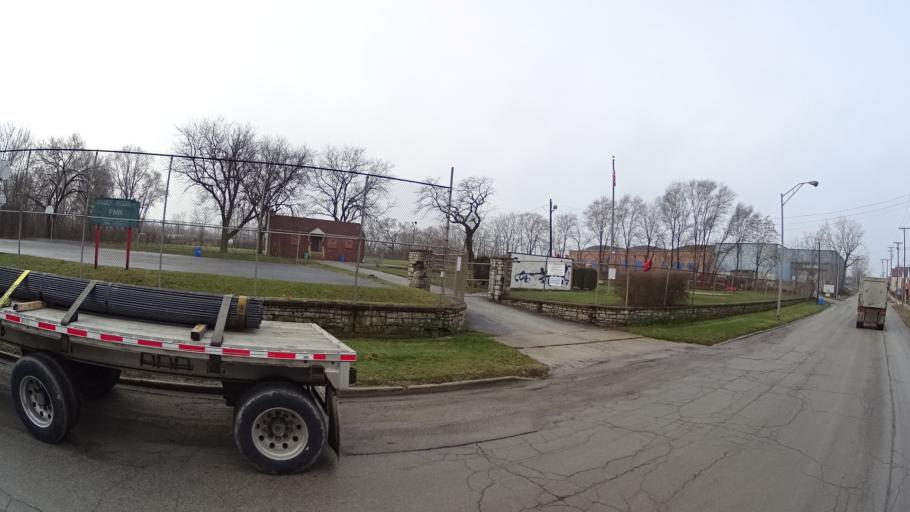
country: US
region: Illinois
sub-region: Cook County
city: Chicago Heights
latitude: 41.5027
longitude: -87.6189
